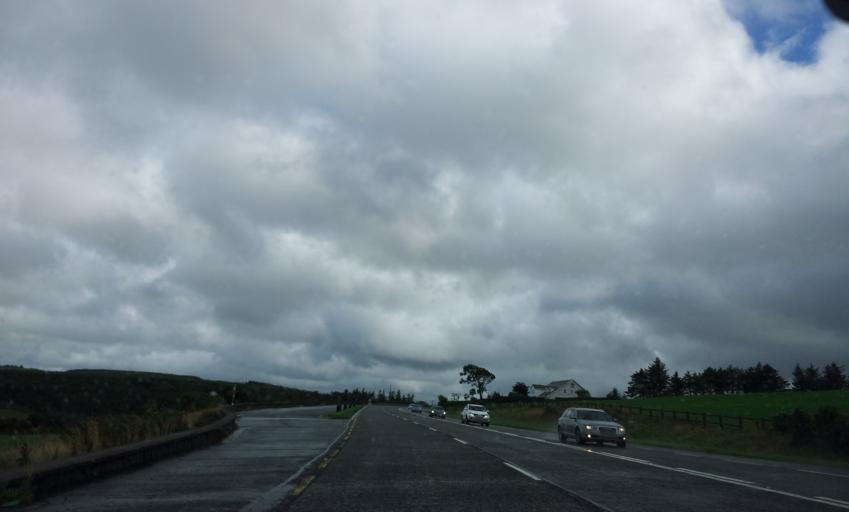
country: IE
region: Munster
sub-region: Waterford
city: Dungarvan
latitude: 52.0526
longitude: -7.6644
